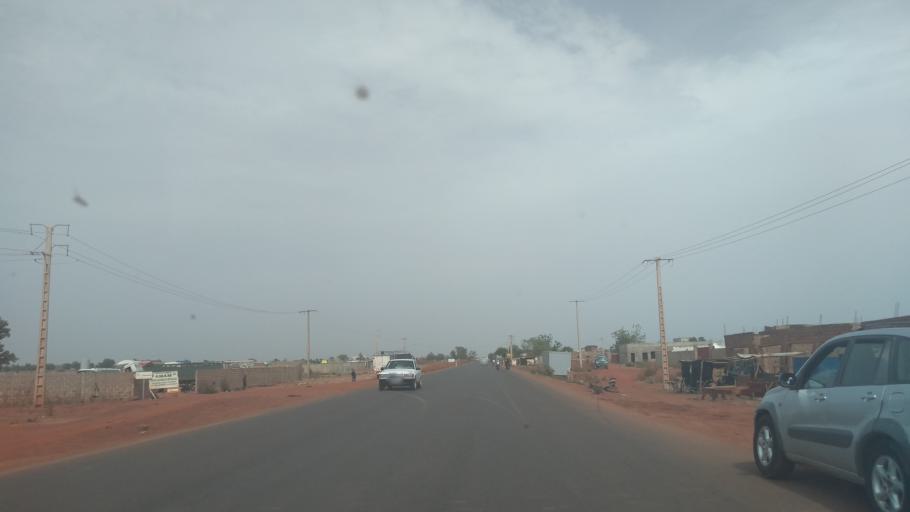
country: ML
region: Bamako
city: Bamako
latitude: 12.5845
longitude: -7.8243
